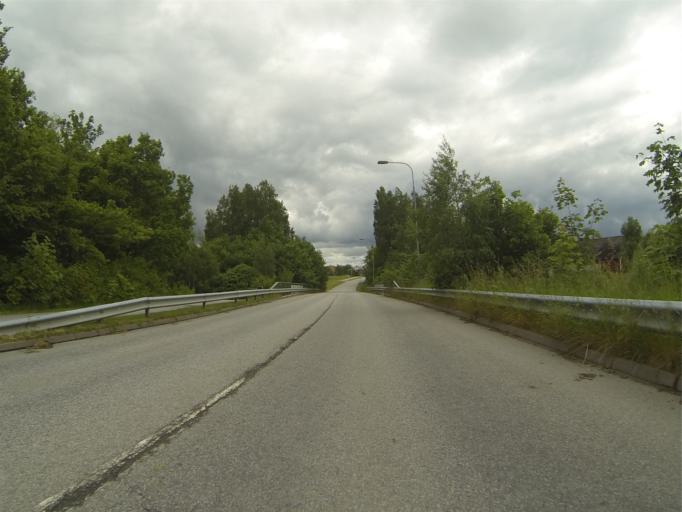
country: SE
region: Skane
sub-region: Lunds Kommun
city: Genarp
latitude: 55.6649
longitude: 13.3591
